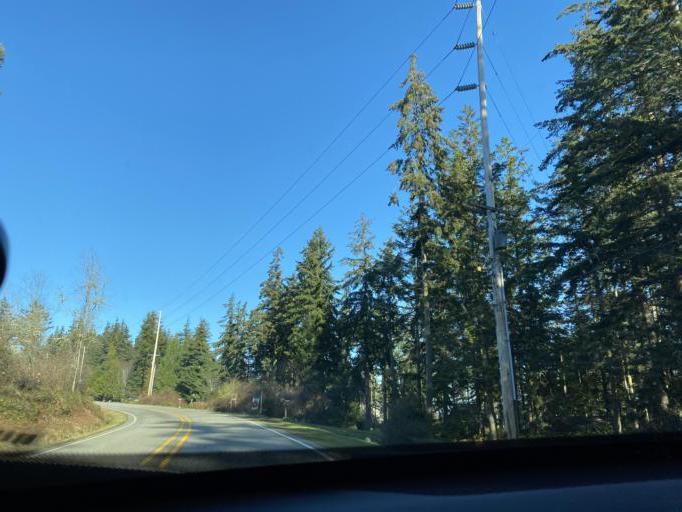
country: US
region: Washington
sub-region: Island County
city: Camano
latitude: 48.1144
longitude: -122.5613
